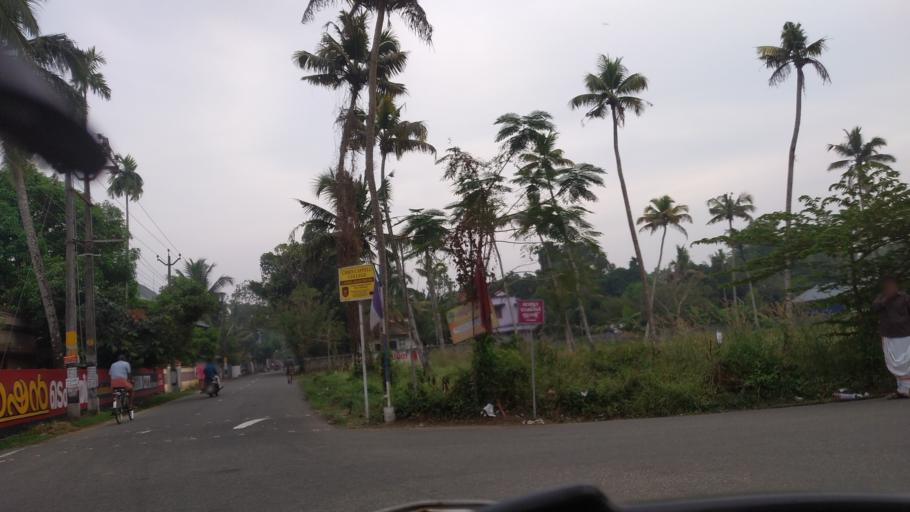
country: IN
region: Kerala
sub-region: Ernakulam
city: Elur
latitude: 10.1454
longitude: 76.2465
